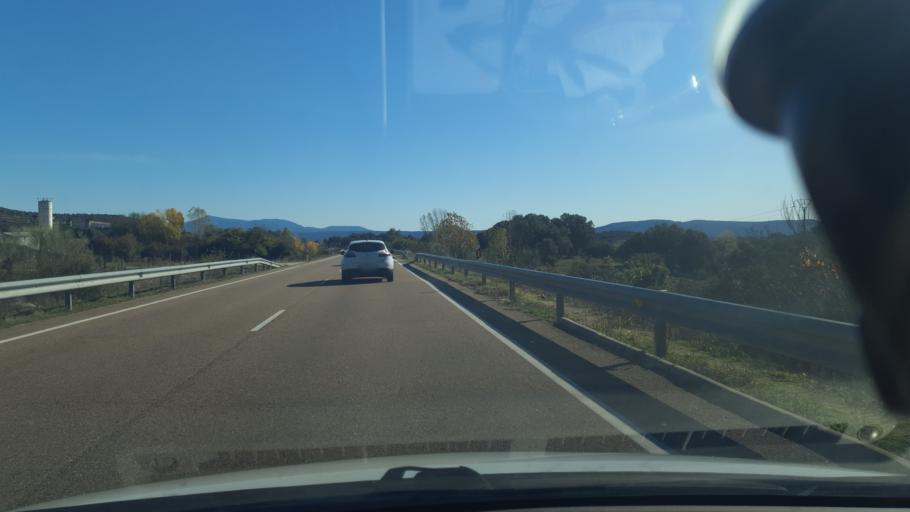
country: ES
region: Castille and Leon
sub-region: Provincia de Avila
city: Arenas de San Pedro
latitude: 40.1873
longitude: -5.0610
